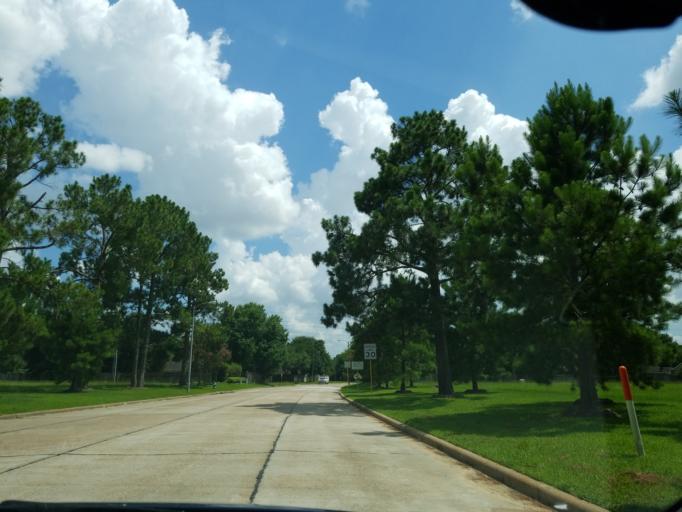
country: US
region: Texas
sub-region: Harris County
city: Cypress
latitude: 29.8787
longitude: -95.7319
